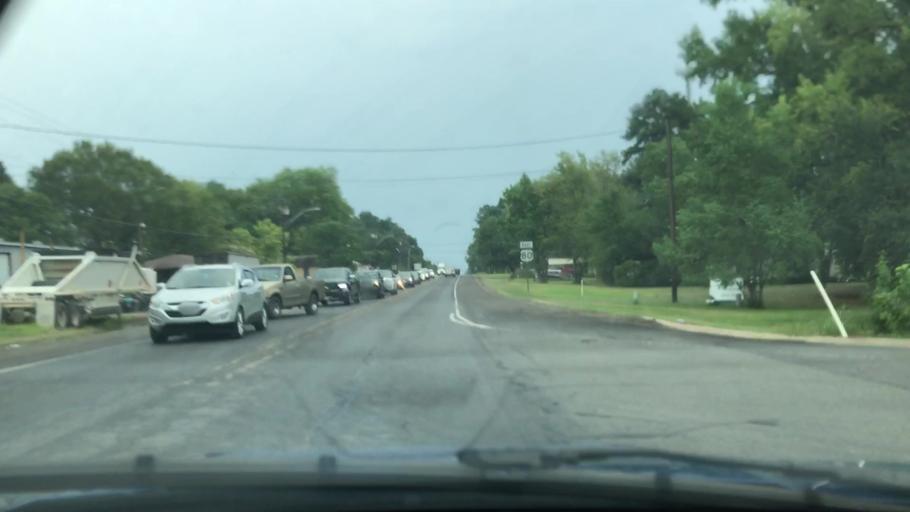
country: US
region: Texas
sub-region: Harrison County
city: Waskom
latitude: 32.4762
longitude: -94.0523
